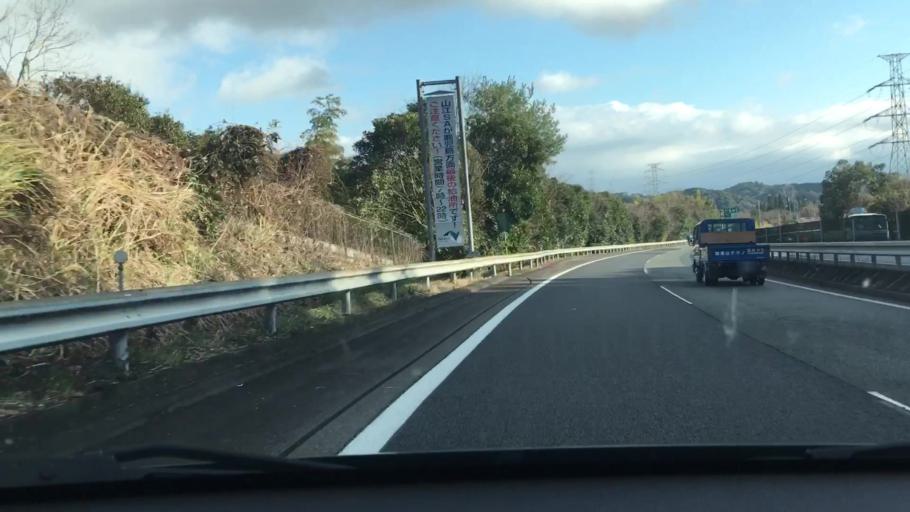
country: JP
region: Kumamoto
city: Hitoyoshi
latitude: 32.2658
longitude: 130.7654
